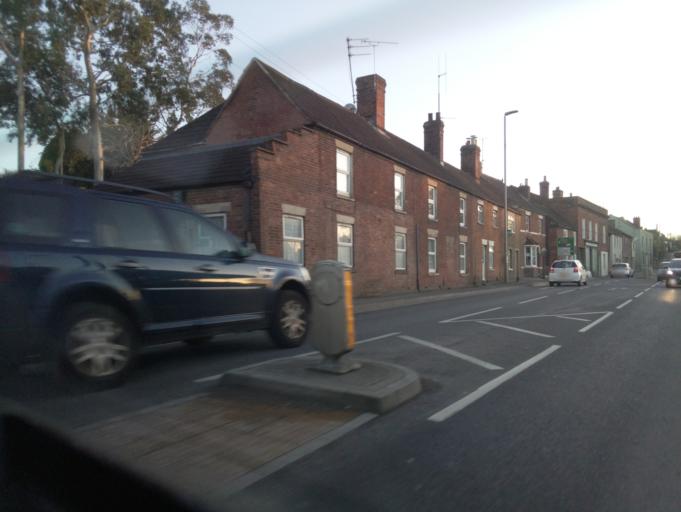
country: GB
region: England
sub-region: Wiltshire
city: Westbury
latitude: 51.2576
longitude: -2.1851
